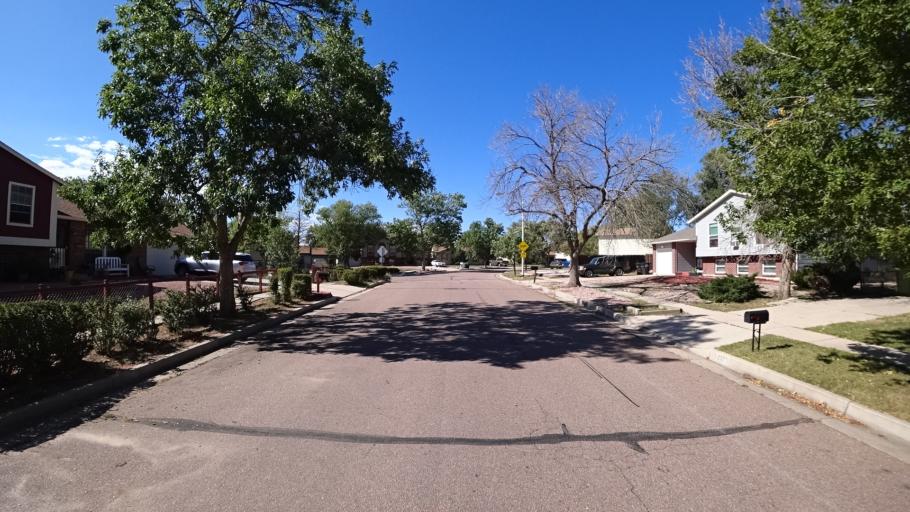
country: US
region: Colorado
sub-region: El Paso County
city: Stratmoor
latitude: 38.7909
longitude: -104.7477
